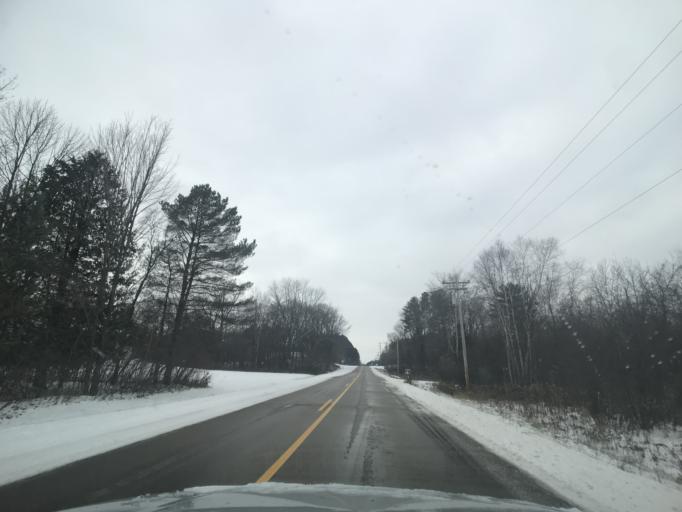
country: US
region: Wisconsin
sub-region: Brown County
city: Suamico
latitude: 44.7063
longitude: -88.0984
